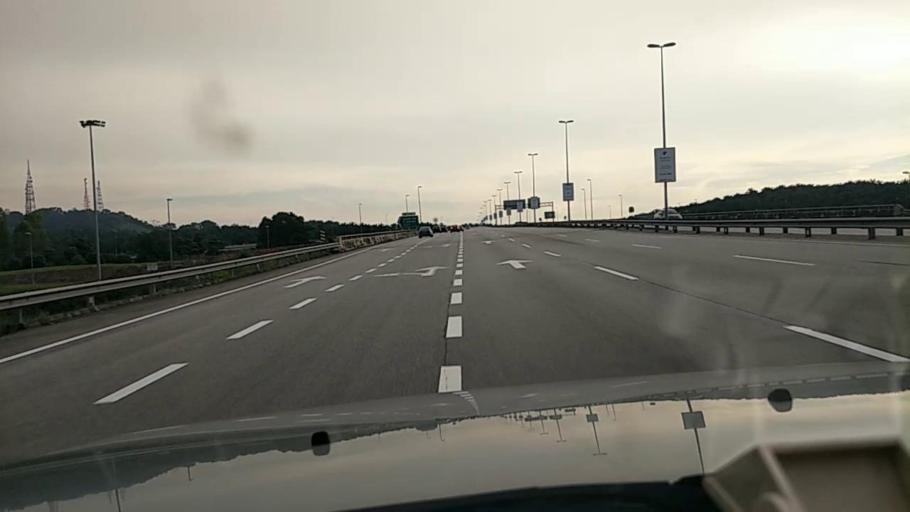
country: MY
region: Selangor
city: Kuang
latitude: 3.2703
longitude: 101.5465
